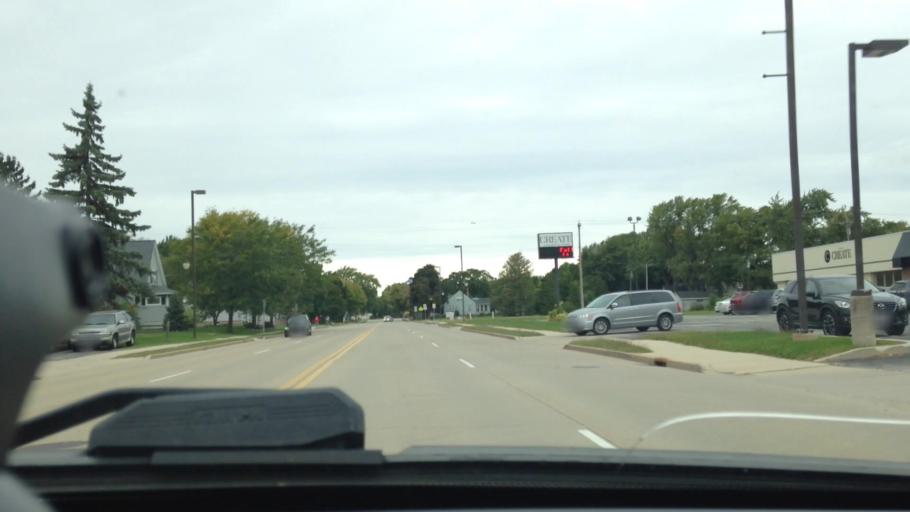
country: US
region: Wisconsin
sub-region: Fond du Lac County
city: North Fond du Lac
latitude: 43.8032
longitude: -88.4803
